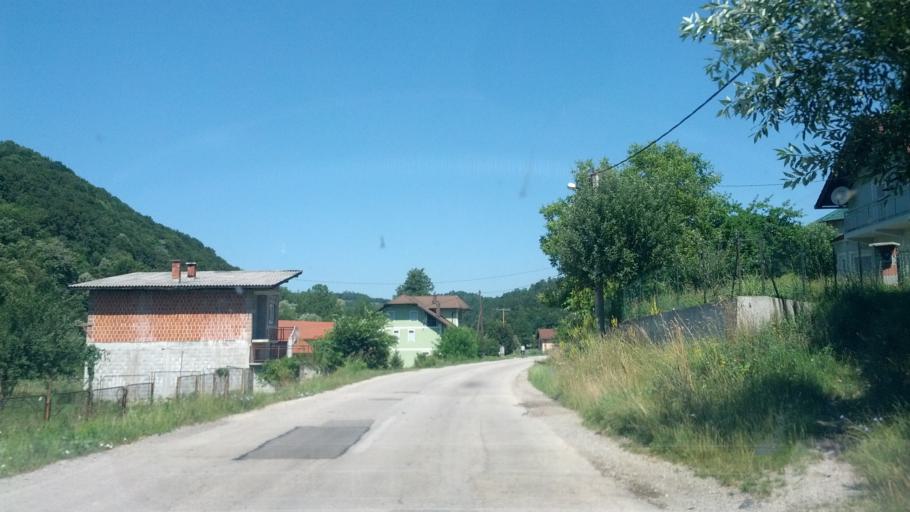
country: BA
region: Federation of Bosnia and Herzegovina
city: Otoka
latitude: 44.9764
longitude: 16.1742
